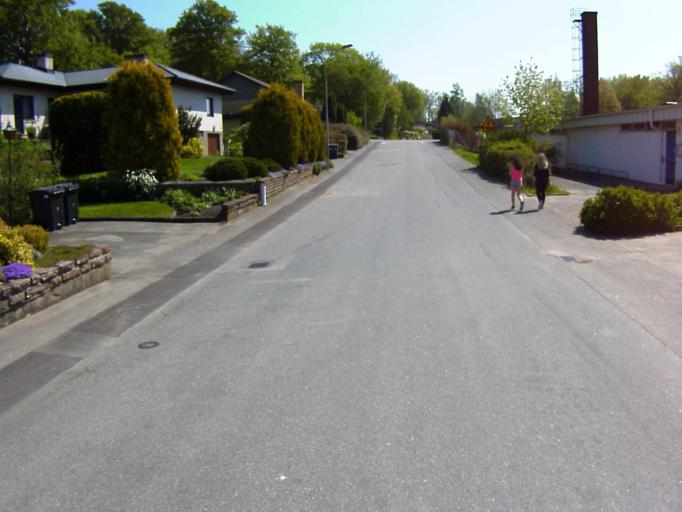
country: SE
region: Skane
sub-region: Kristianstads Kommun
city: Tollarp
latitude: 56.1730
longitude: 14.2869
